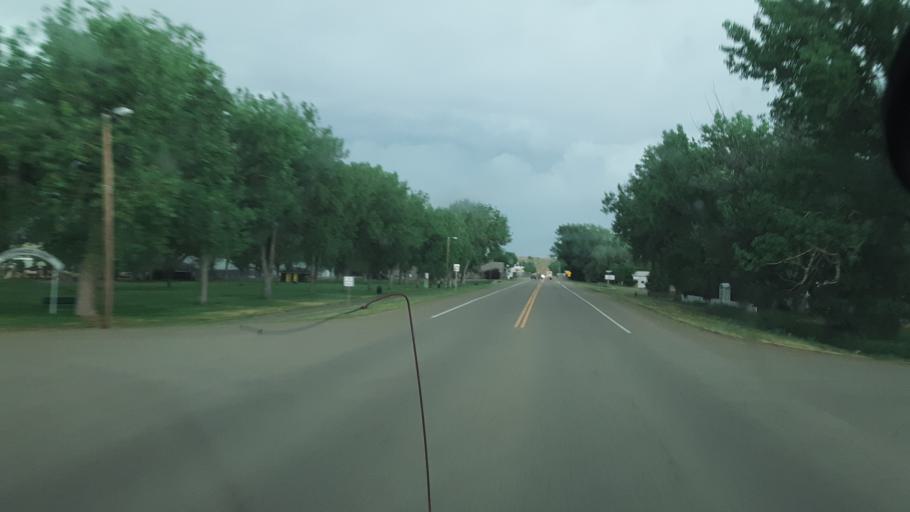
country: US
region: Montana
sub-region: Powder River County
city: Broadus
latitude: 45.4386
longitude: -105.4083
